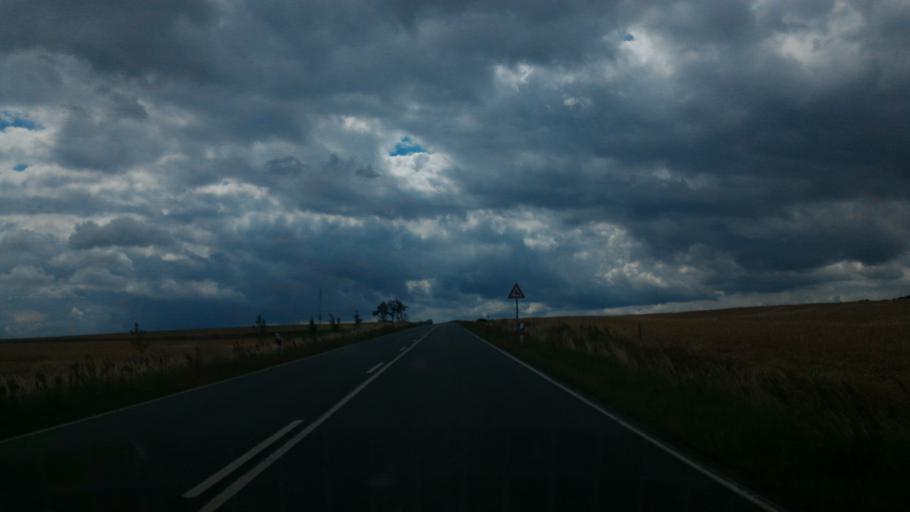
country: DE
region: Saxony
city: Goerlitz
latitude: 51.2009
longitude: 14.9431
